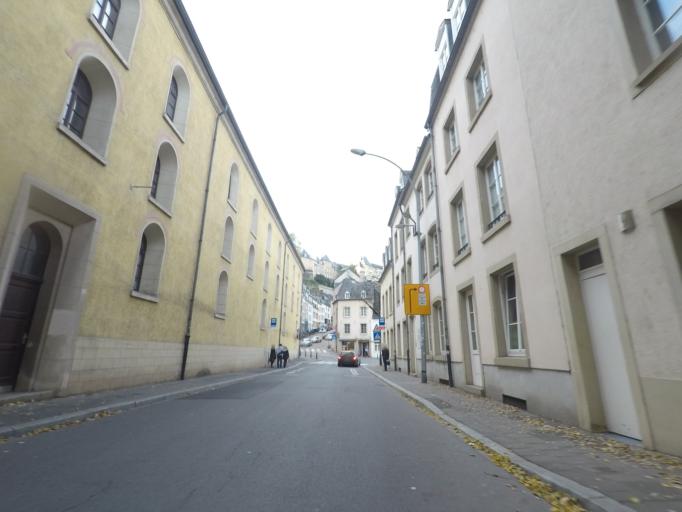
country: LU
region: Luxembourg
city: Itzig
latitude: 49.5930
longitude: 6.1504
